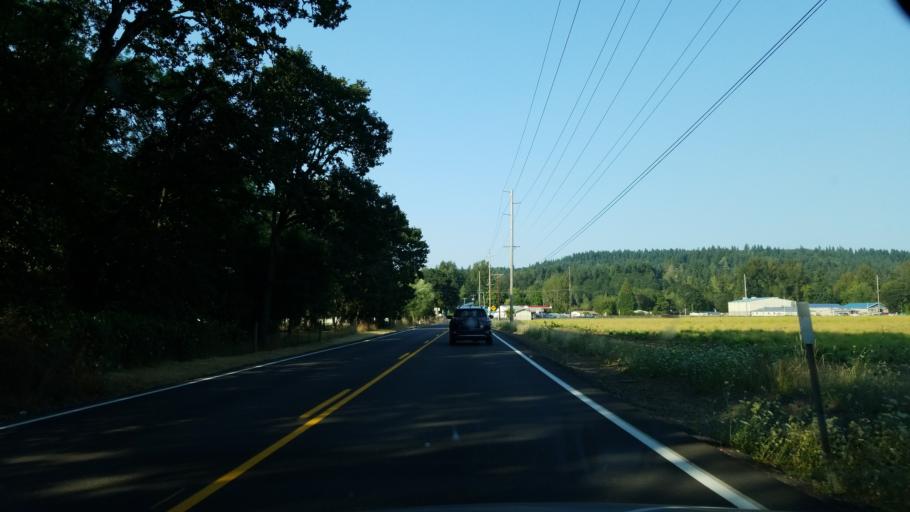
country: US
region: Oregon
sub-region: Clackamas County
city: Molalla
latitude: 45.1694
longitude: -122.5237
